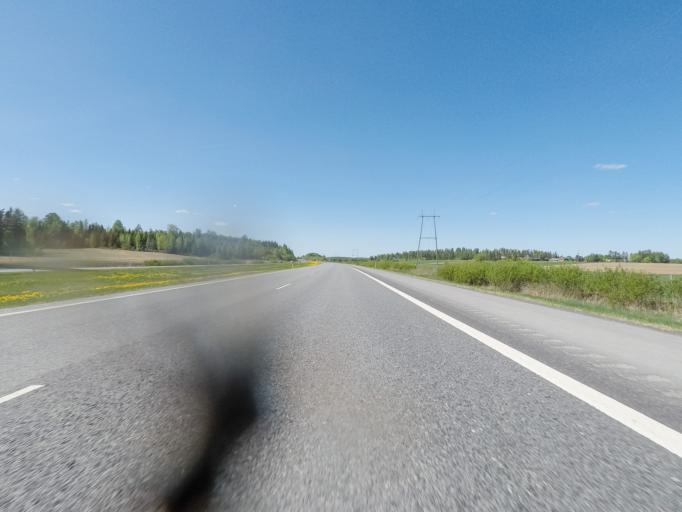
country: FI
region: Pirkanmaa
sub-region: Etelae-Pirkanmaa
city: Akaa
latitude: 61.1707
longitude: 23.9352
